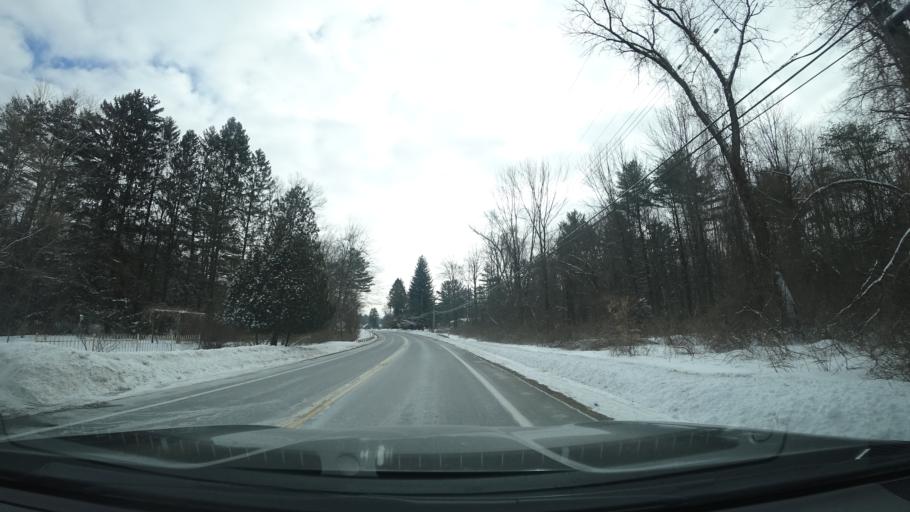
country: US
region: New York
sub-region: Saratoga County
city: South Glens Falls
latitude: 43.2795
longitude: -73.6161
